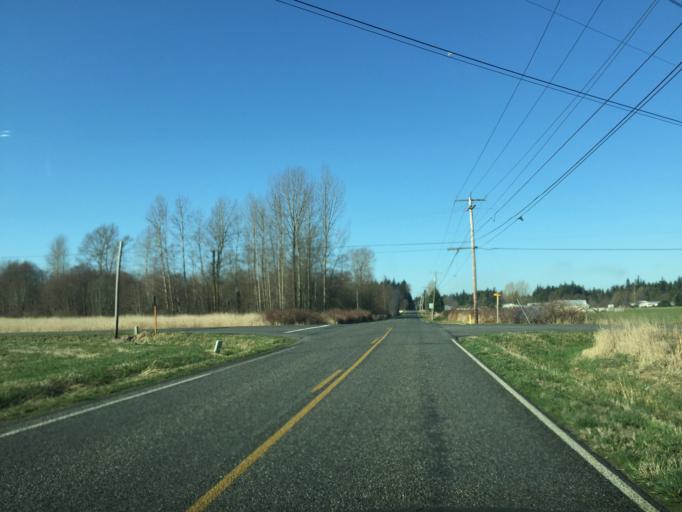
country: US
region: Washington
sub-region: Whatcom County
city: Ferndale
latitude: 48.8553
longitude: -122.5184
